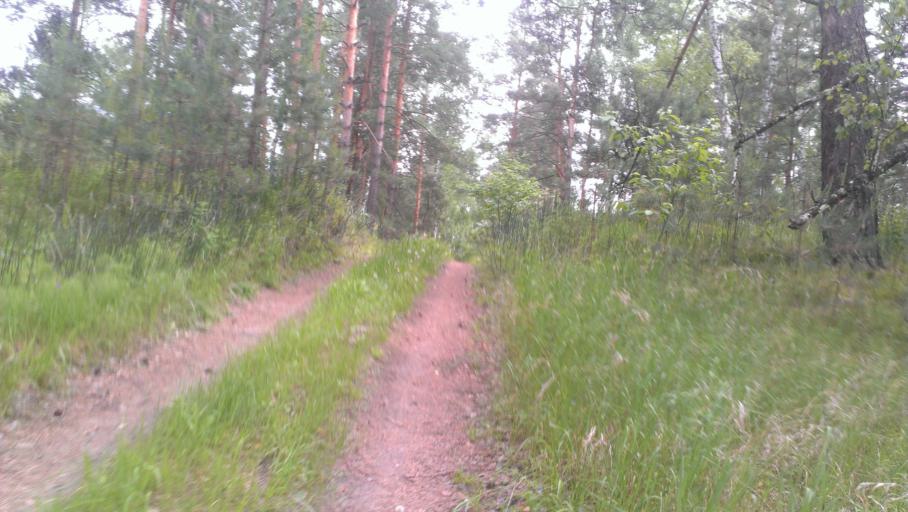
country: RU
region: Altai Krai
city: Sannikovo
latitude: 53.3477
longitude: 84.0397
